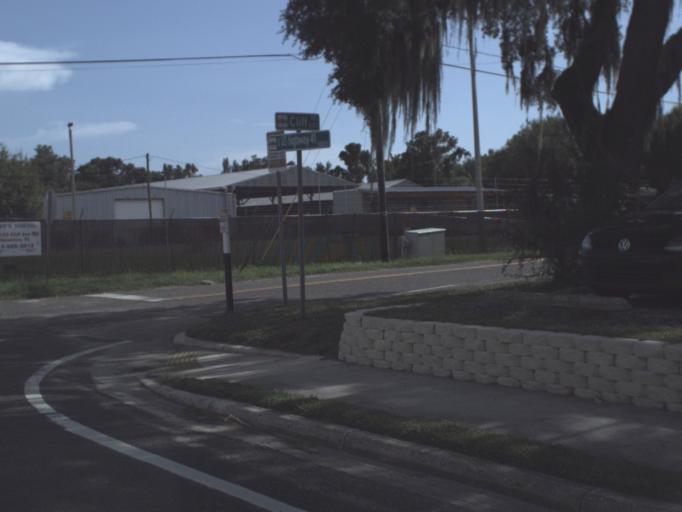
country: US
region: Florida
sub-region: Hillsborough County
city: Gibsonton
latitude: 27.8440
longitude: -82.3817
